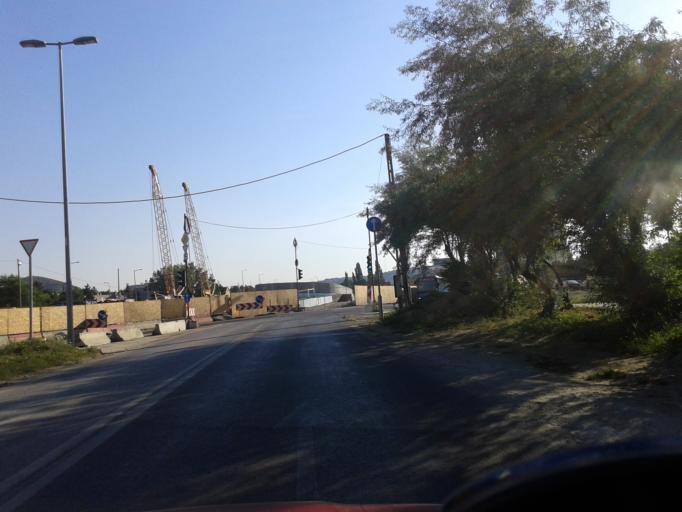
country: HU
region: Budapest
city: Budapest XI. keruelet
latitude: 47.4646
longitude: 19.0144
